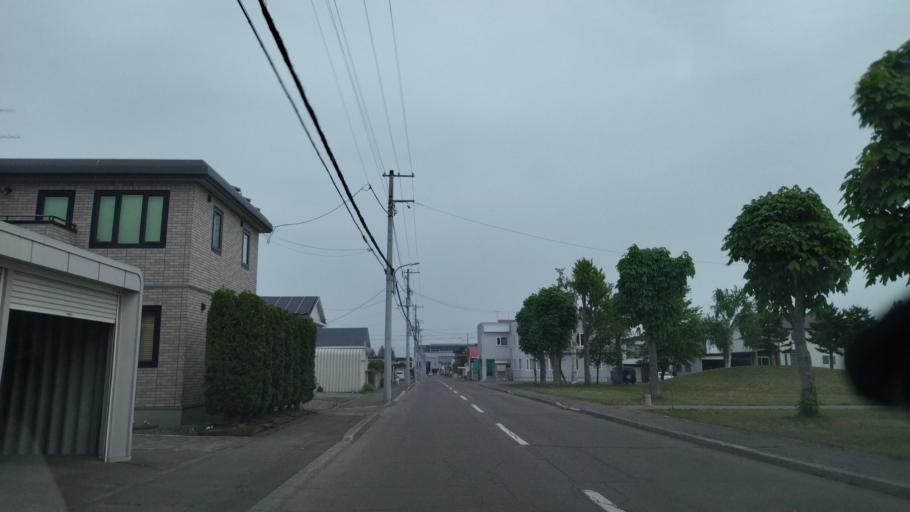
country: JP
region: Hokkaido
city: Obihiro
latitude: 42.9144
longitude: 143.0517
